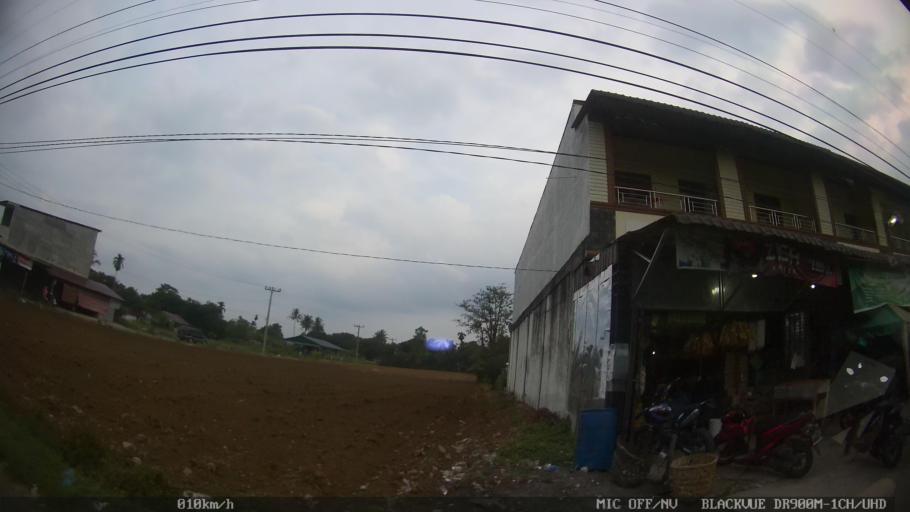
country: ID
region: North Sumatra
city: Sunggal
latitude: 3.5609
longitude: 98.5836
